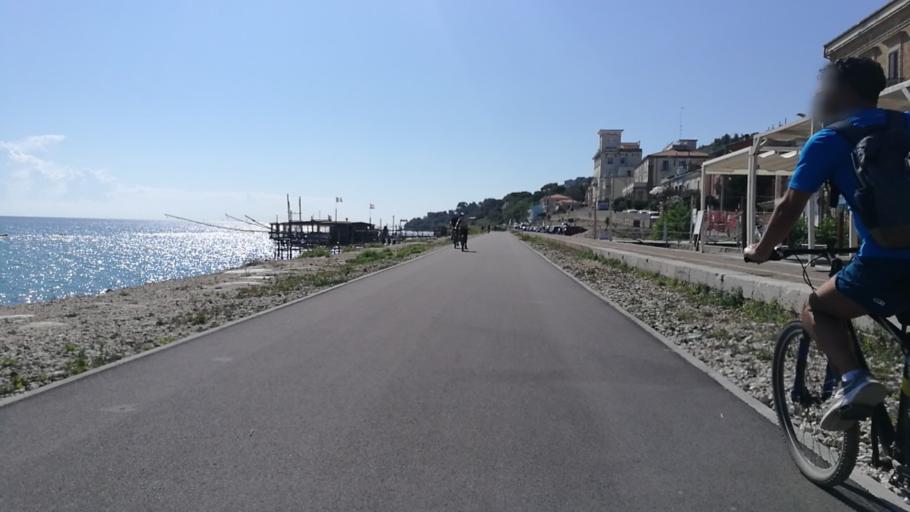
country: IT
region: Abruzzo
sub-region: Provincia di Chieti
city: Marina di San Vito
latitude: 42.3065
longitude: 14.4494
